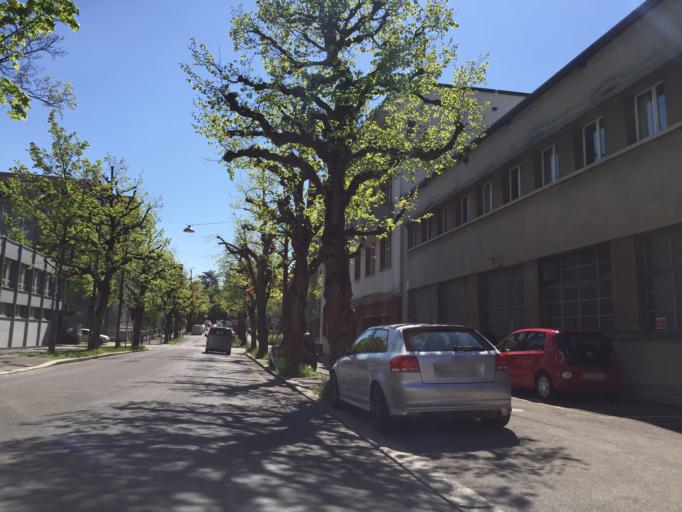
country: CH
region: Bern
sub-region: Bern-Mittelland District
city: Bern
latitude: 46.9549
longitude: 7.4529
